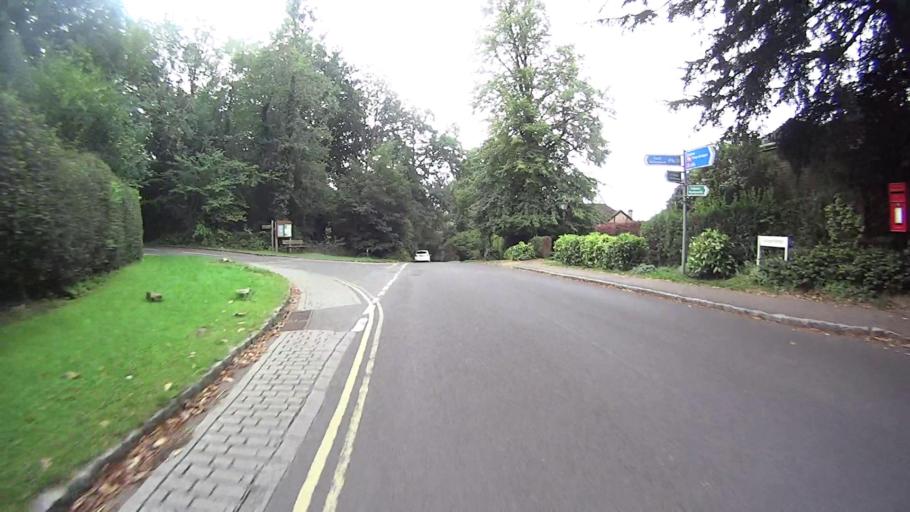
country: GB
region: England
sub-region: West Sussex
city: Maidenbower
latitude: 51.1111
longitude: -0.1437
